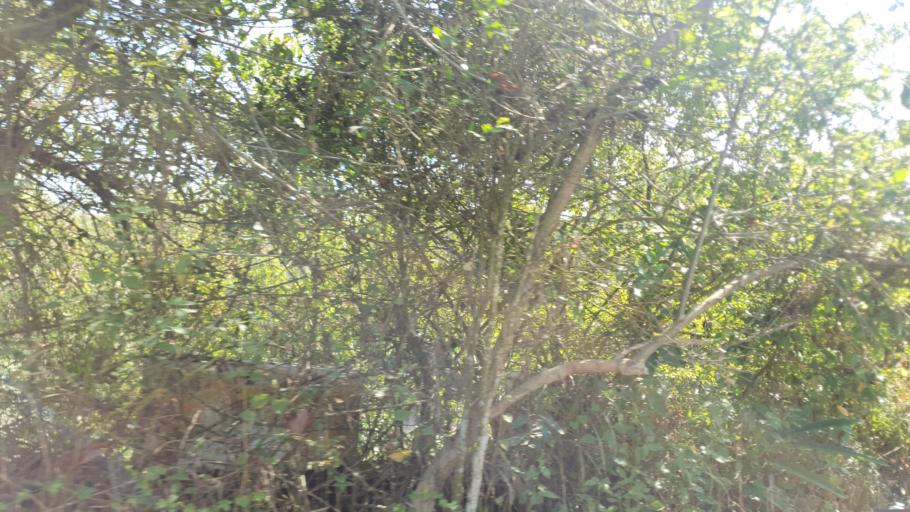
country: TW
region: Taiwan
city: Yujing
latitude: 23.0482
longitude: 120.3733
